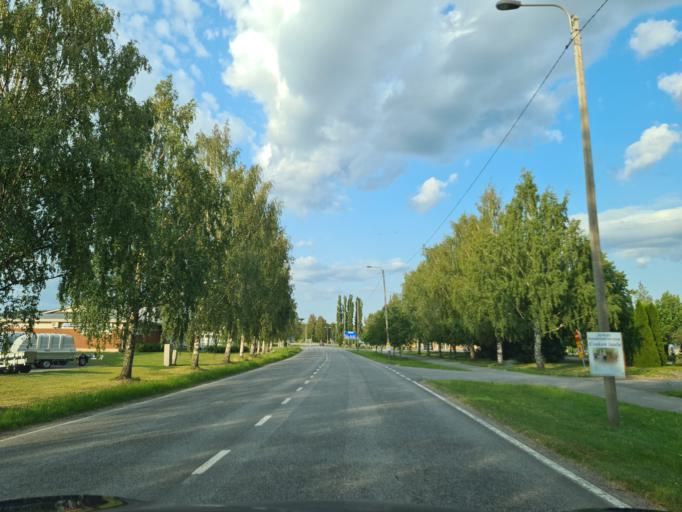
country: FI
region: Southern Ostrobothnia
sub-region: Seinaejoki
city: Lapua
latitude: 62.9750
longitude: 23.0184
